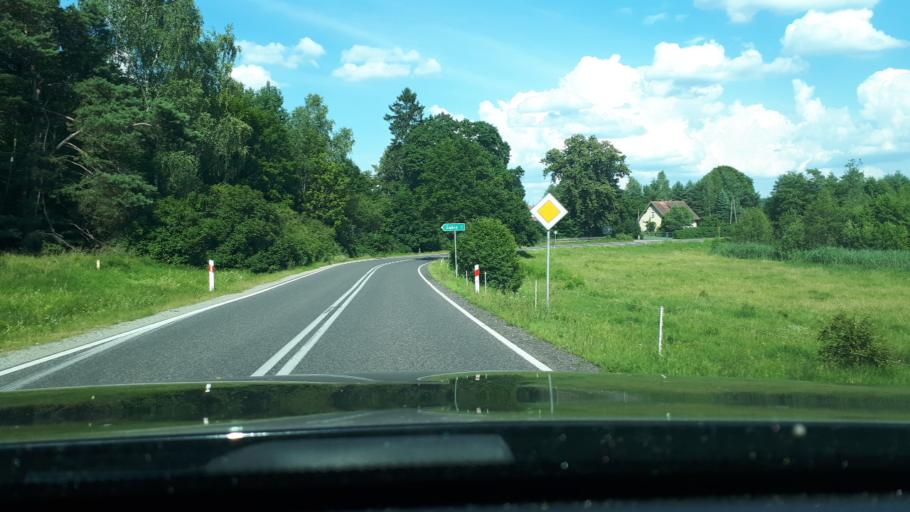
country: PL
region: Warmian-Masurian Voivodeship
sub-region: Powiat olsztynski
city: Stawiguda
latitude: 53.5384
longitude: 20.4706
